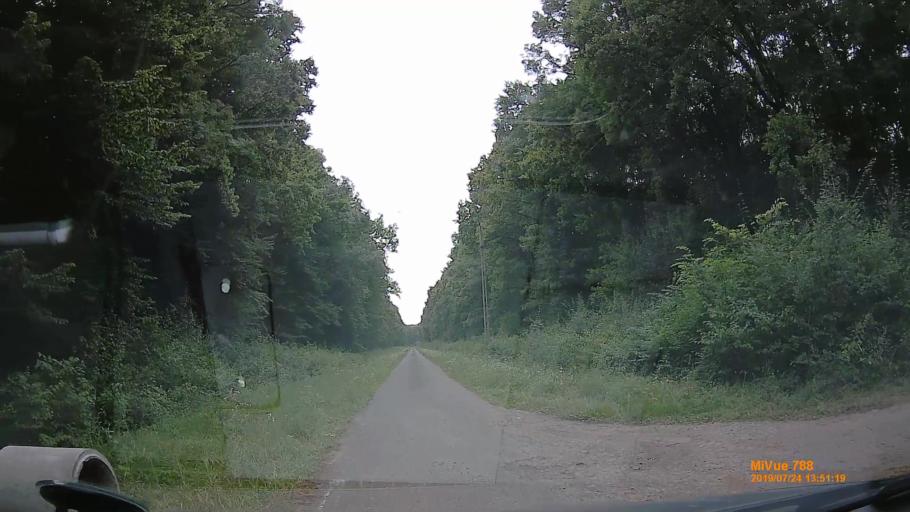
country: HU
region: Szabolcs-Szatmar-Bereg
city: Aranyosapati
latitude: 48.2687
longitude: 22.3448
